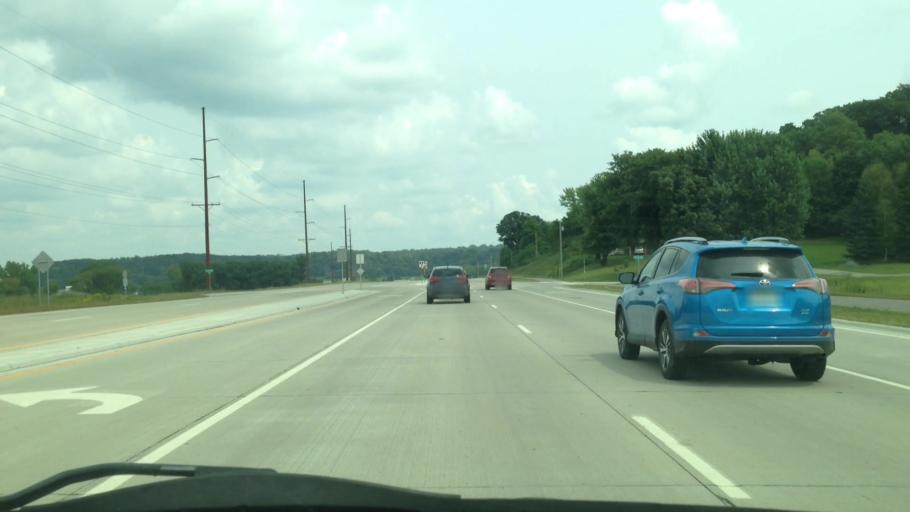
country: US
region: Minnesota
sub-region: Olmsted County
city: Rochester
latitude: 44.0641
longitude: -92.4517
